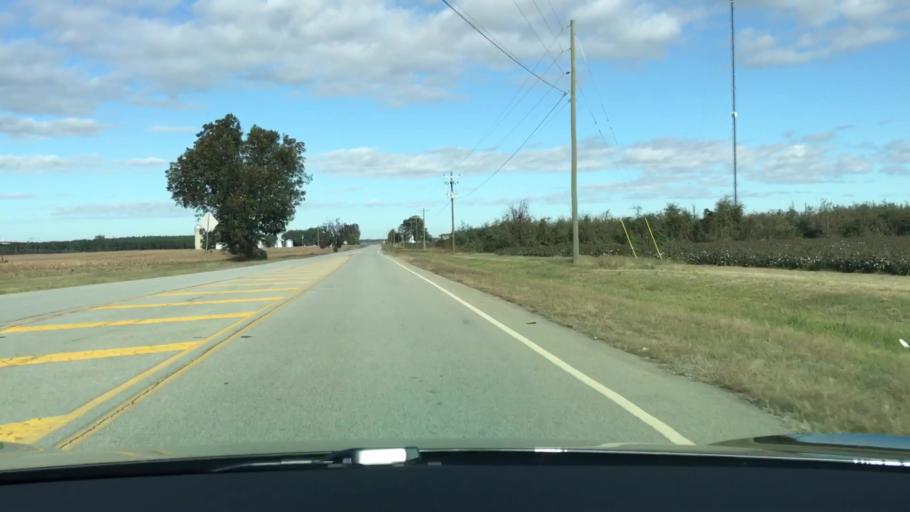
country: US
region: Georgia
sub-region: Jefferson County
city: Louisville
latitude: 33.1021
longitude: -82.4233
